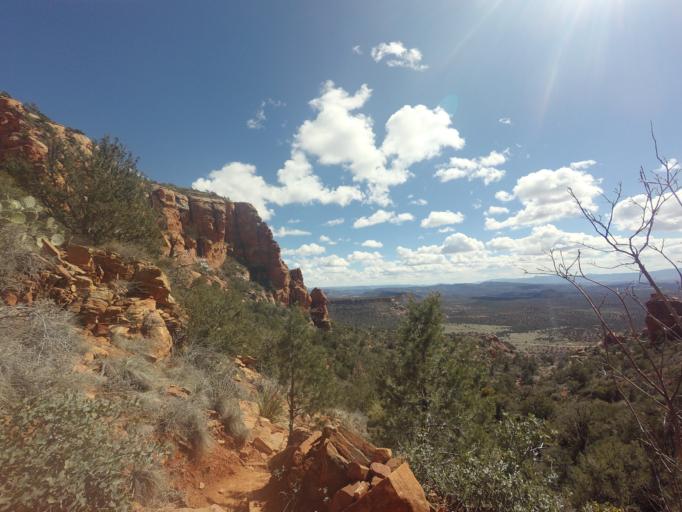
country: US
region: Arizona
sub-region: Yavapai County
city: West Sedona
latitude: 34.9032
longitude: -111.8731
